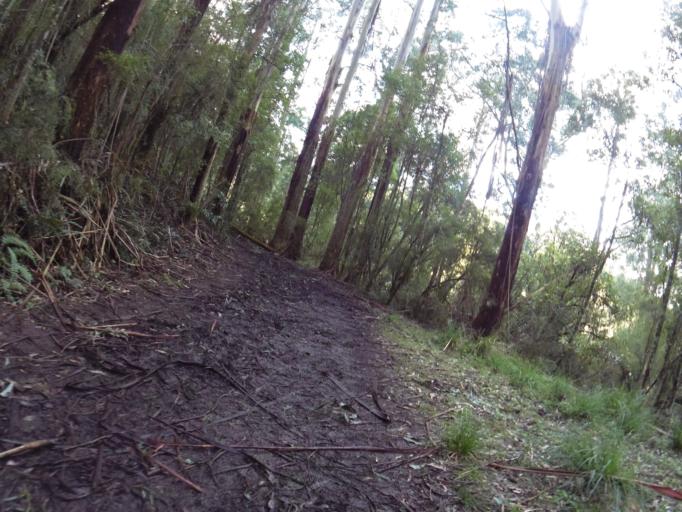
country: AU
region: Victoria
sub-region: Yarra Ranges
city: Belgrave
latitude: -37.8912
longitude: 145.3528
